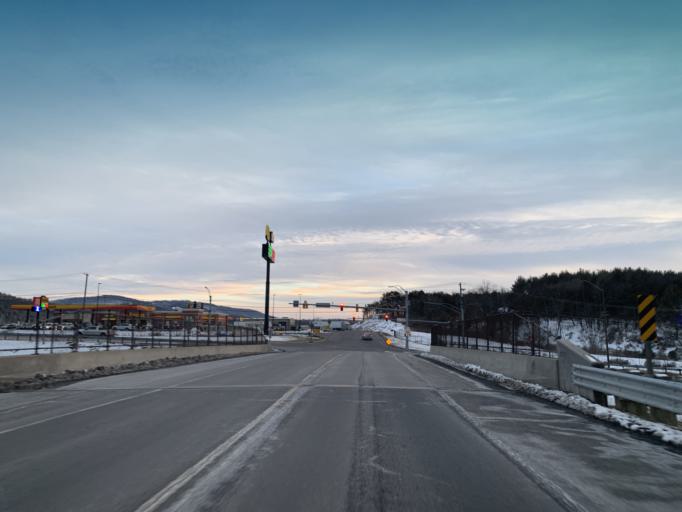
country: US
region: Maryland
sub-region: Allegany County
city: Cumberland
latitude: 39.6741
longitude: -78.7172
